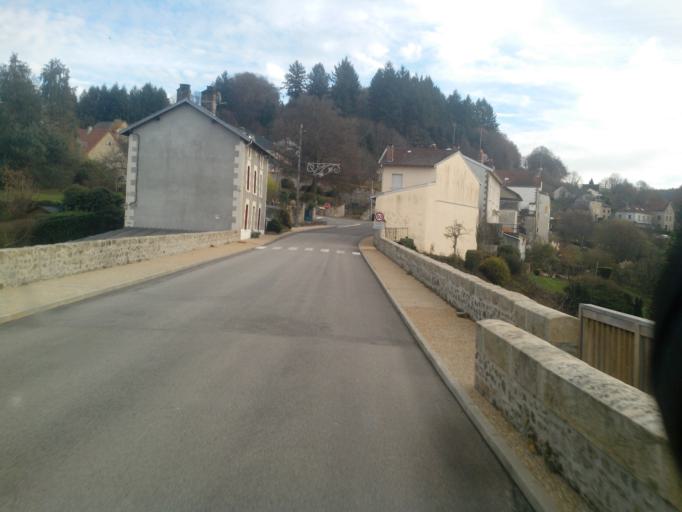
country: FR
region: Limousin
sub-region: Departement de la Haute-Vienne
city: Eymoutiers
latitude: 45.7371
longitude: 1.7460
